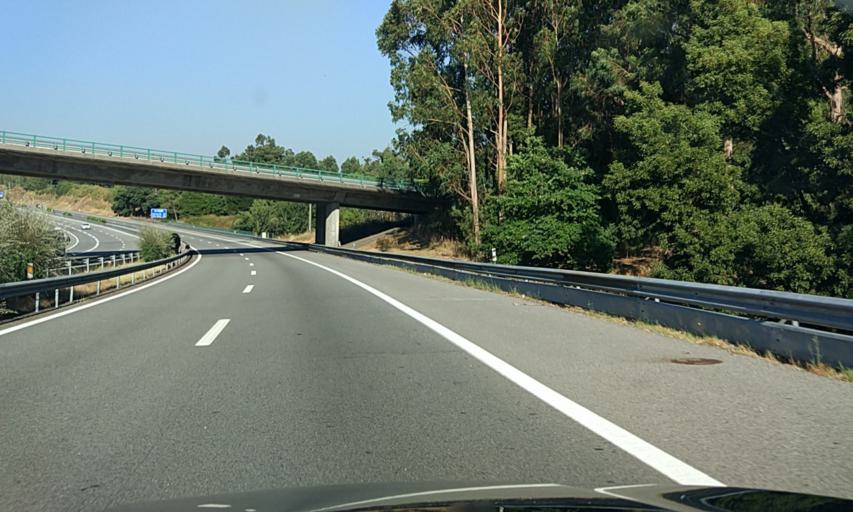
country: PT
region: Porto
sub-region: Lousada
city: Meinedo
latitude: 41.2326
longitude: -8.2019
